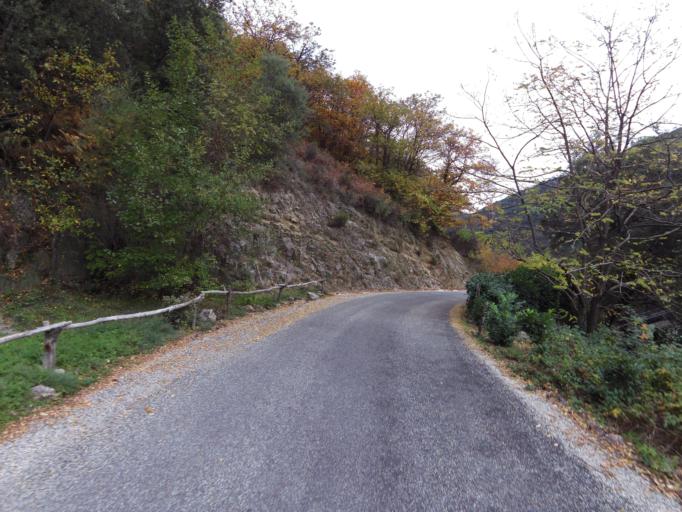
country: FR
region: Rhone-Alpes
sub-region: Departement de l'Ardeche
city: Les Vans
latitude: 44.4951
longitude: 4.0429
